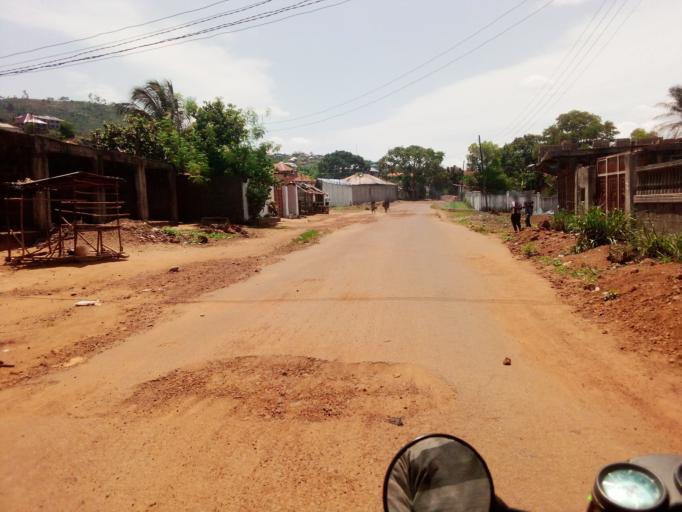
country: SL
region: Western Area
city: Waterloo
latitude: 8.3337
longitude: -13.0744
